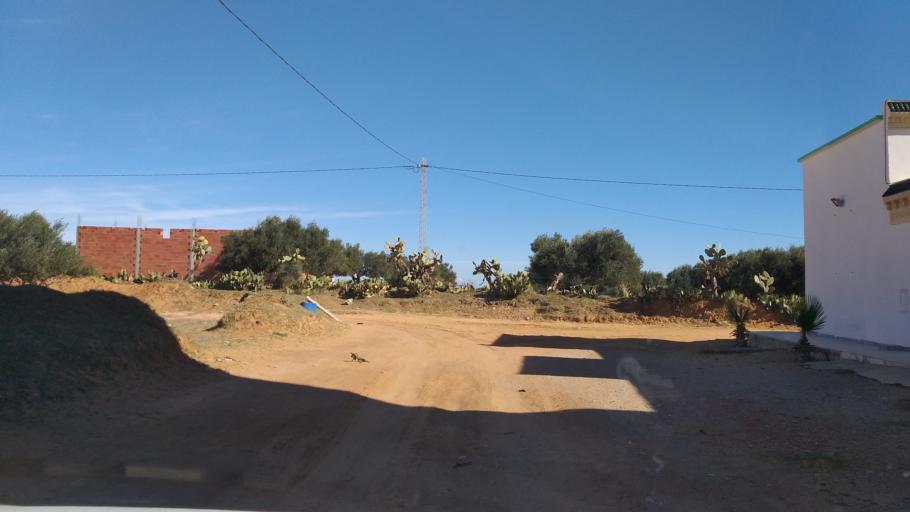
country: TN
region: Al Mahdiyah
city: El Jem
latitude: 35.2548
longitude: 10.6090
